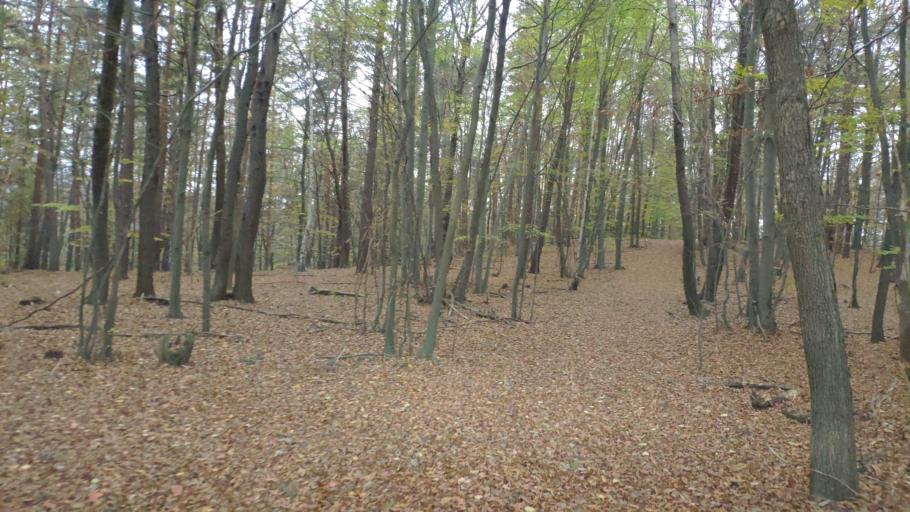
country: SK
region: Presovsky
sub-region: Okres Presov
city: Presov
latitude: 48.9409
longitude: 21.1022
